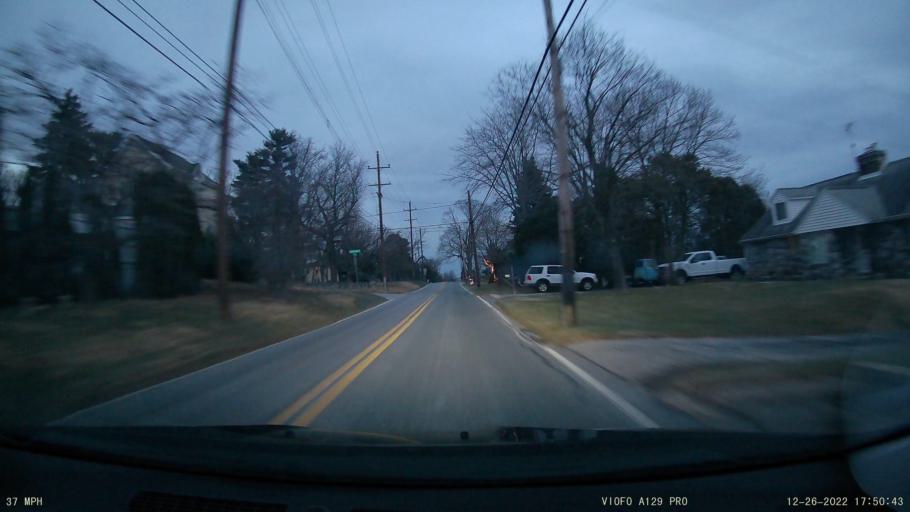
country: US
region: Pennsylvania
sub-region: Montgomery County
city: Bridgeport
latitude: 40.1047
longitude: -75.3619
